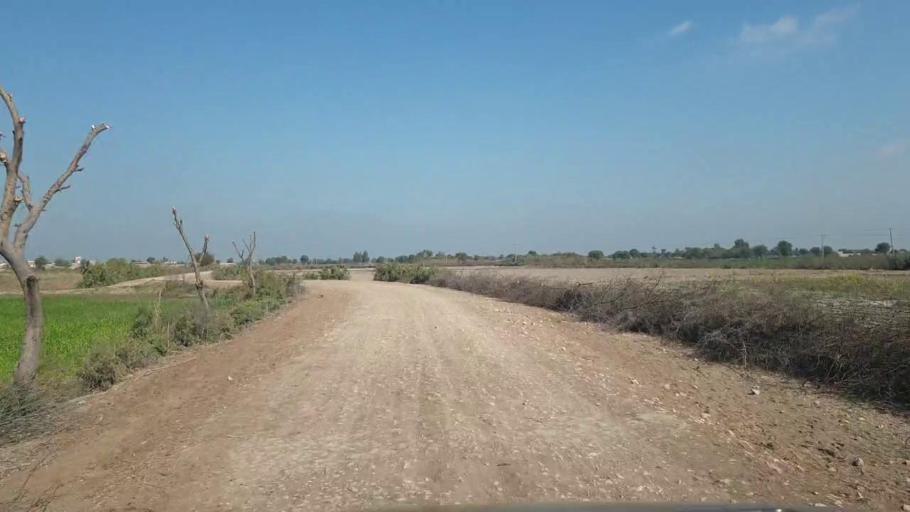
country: PK
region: Sindh
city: Bhit Shah
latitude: 25.8785
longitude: 68.5268
